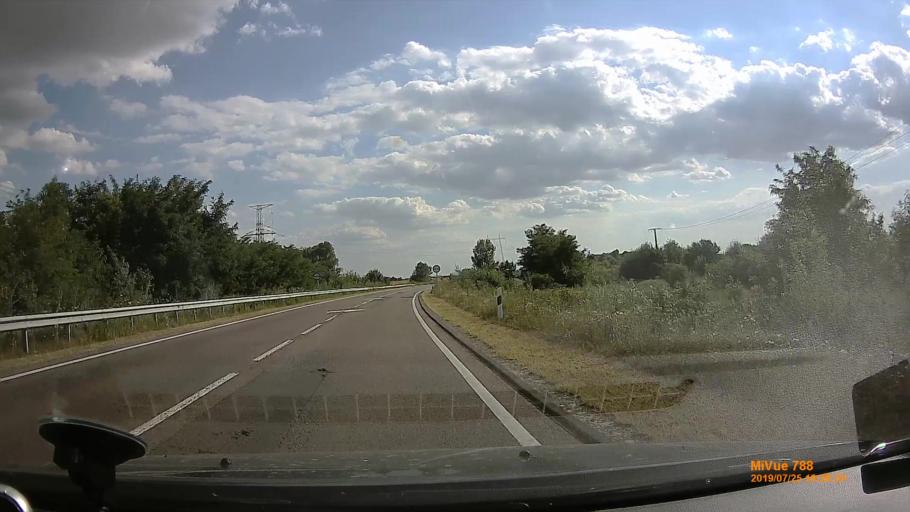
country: HU
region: Heves
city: Karacsond
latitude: 47.7330
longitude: 20.0800
